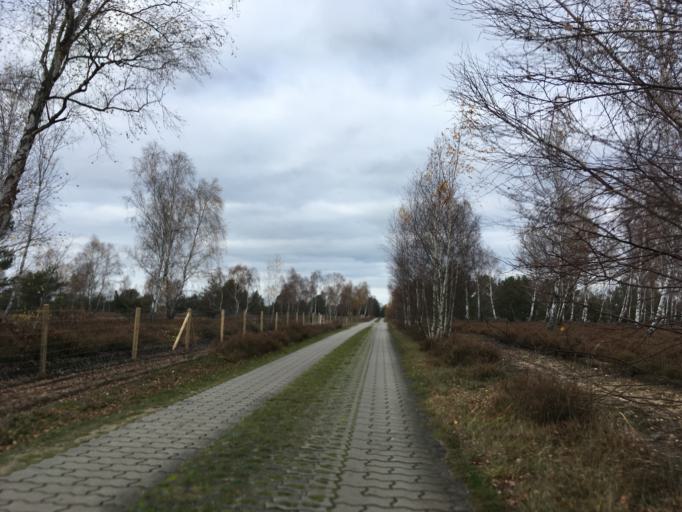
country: DE
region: Brandenburg
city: Tauer
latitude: 52.0034
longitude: 14.5036
